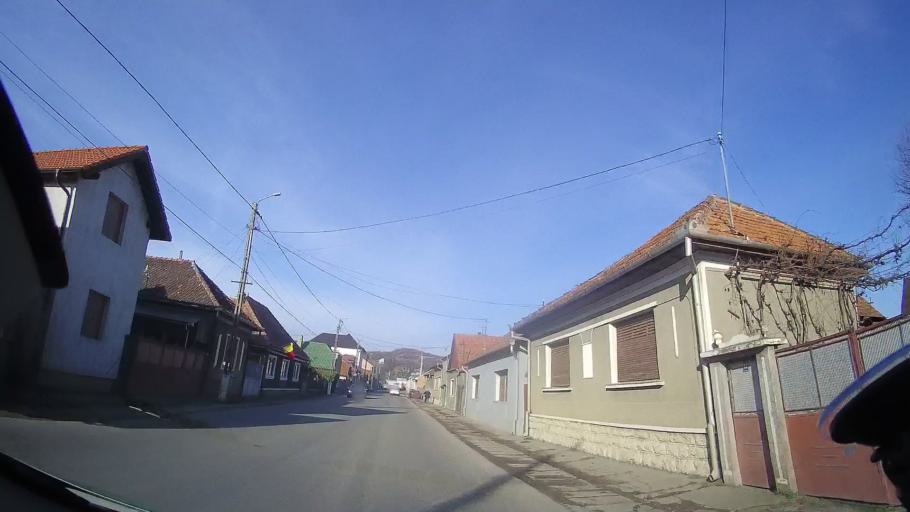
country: RO
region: Bihor
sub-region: Comuna Astileu
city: Astileu
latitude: 47.0578
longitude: 22.3910
